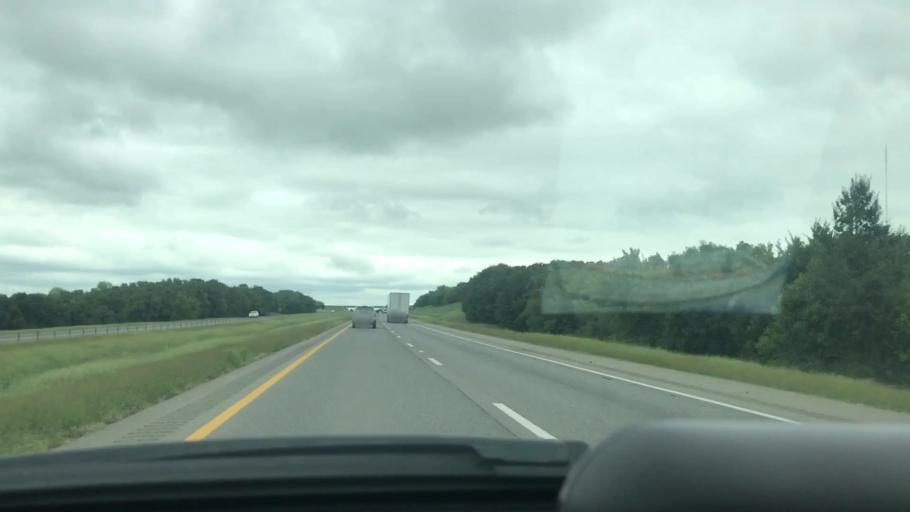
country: US
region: Oklahoma
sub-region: McIntosh County
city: Checotah
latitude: 35.3959
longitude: -95.5639
